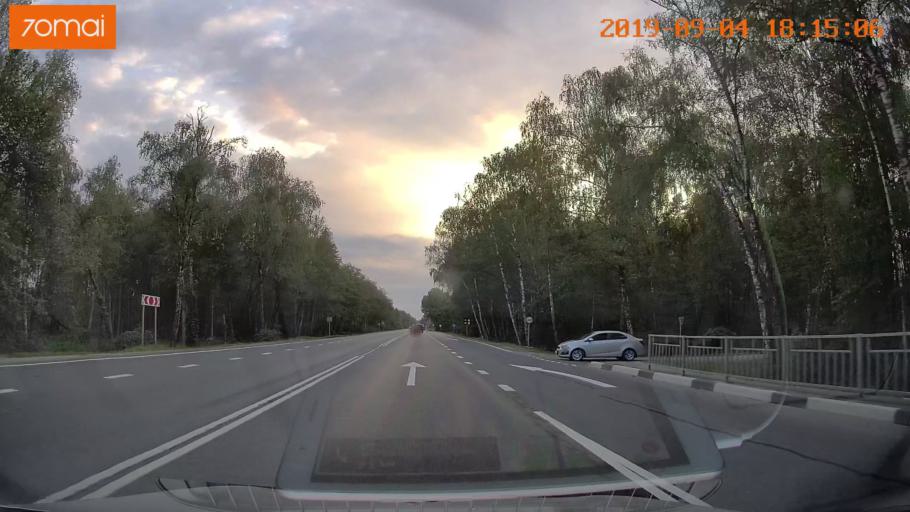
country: RU
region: Moskovskaya
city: Lopatinskiy
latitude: 55.3488
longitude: 38.7095
